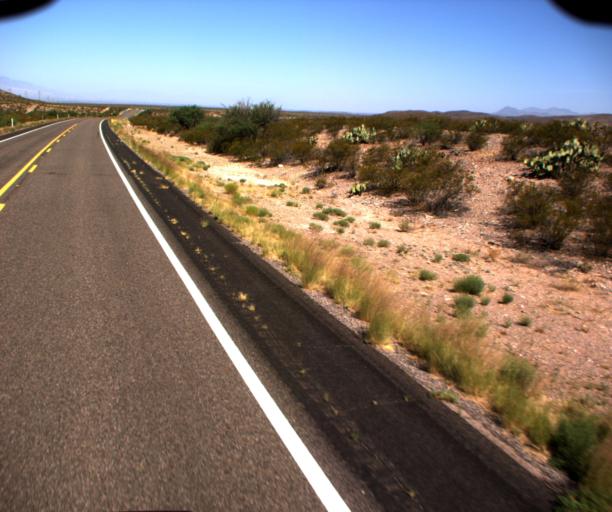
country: US
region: Arizona
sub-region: Greenlee County
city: Clifton
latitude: 32.7499
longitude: -109.3962
